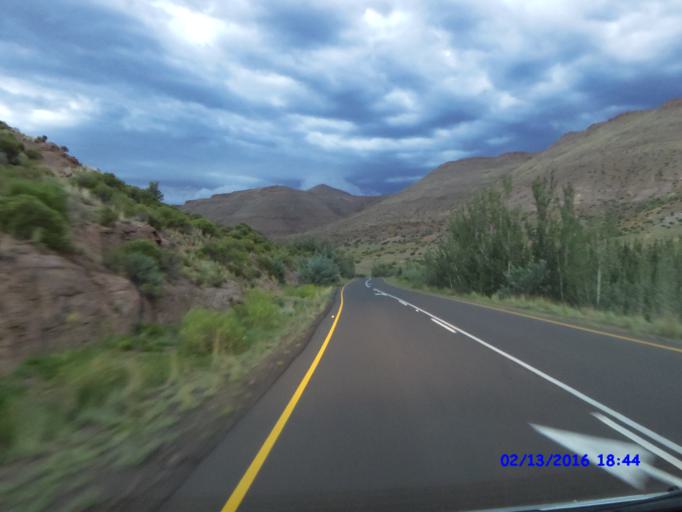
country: LS
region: Qacha's Nek
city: Qacha's Nek
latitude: -30.0537
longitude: 28.3036
